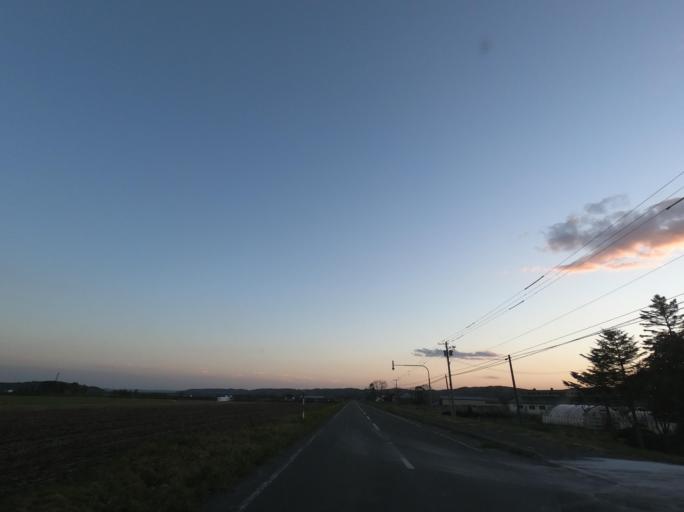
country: JP
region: Hokkaido
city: Kushiro
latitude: 43.2114
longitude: 144.4294
